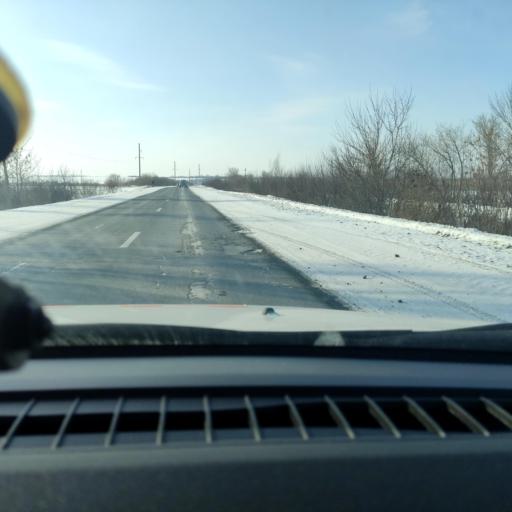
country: RU
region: Samara
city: Smyshlyayevka
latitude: 53.1551
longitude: 50.4298
